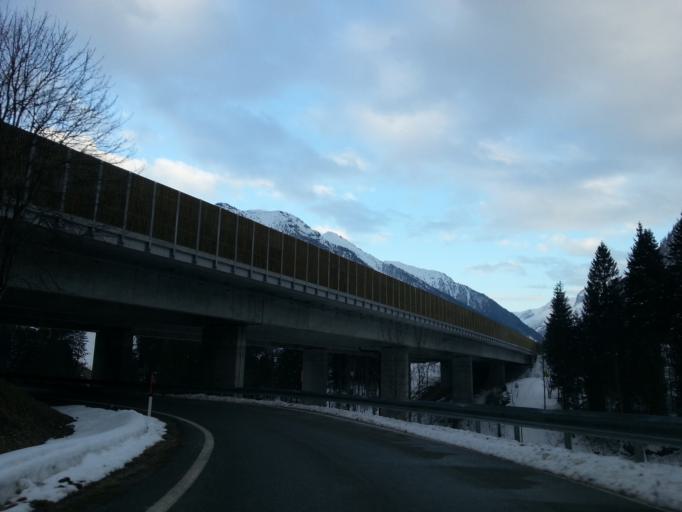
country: AT
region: Salzburg
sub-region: Politischer Bezirk Sankt Johann im Pongau
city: Flachau
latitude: 47.2964
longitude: 13.3931
